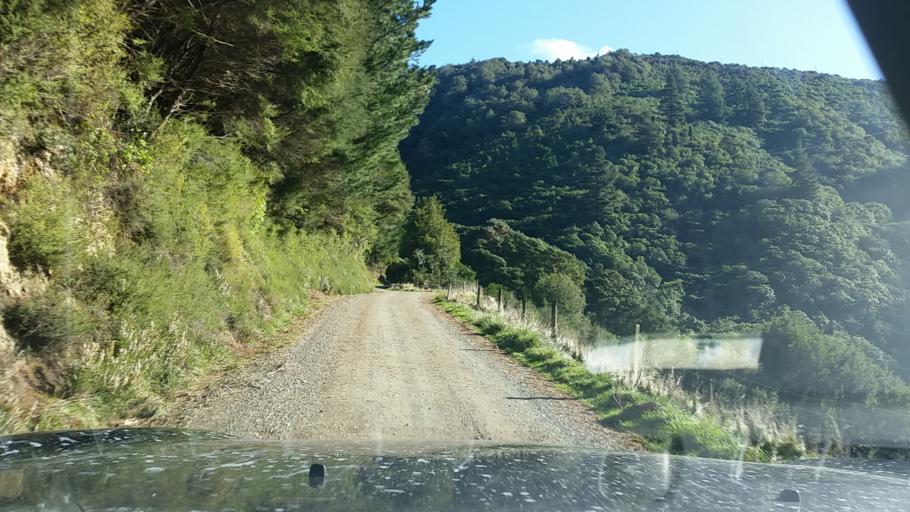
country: NZ
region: Marlborough
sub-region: Marlborough District
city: Picton
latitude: -41.1428
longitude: 174.0504
